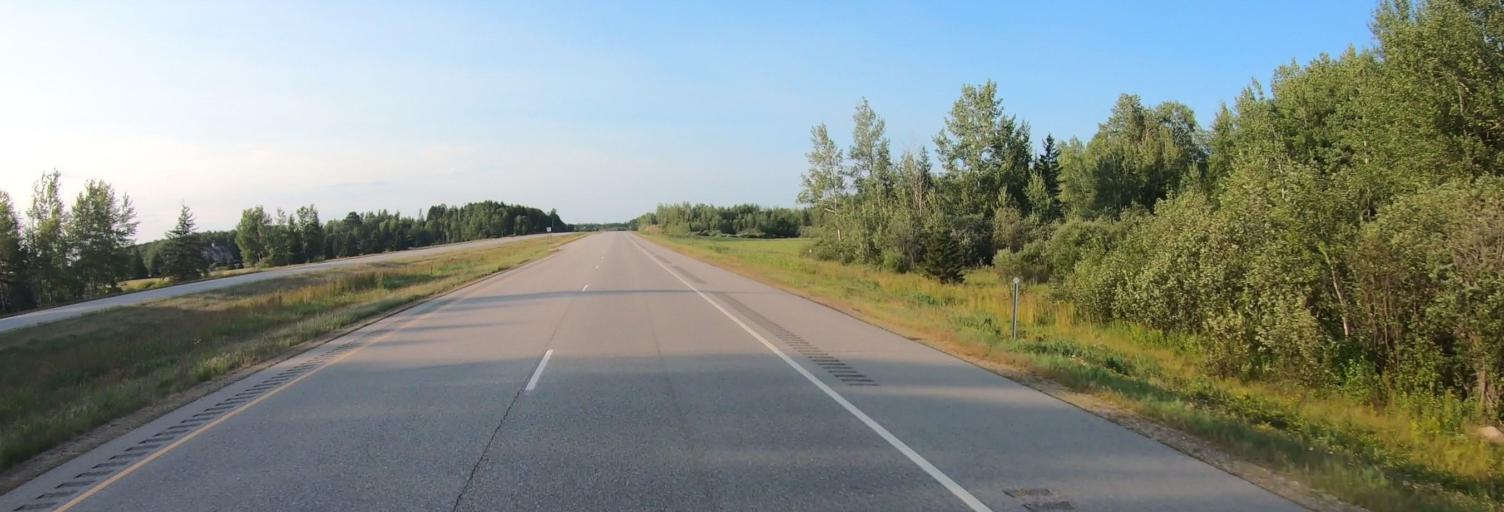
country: US
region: Minnesota
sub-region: Saint Louis County
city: Mountain Iron
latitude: 47.7223
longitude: -92.6509
